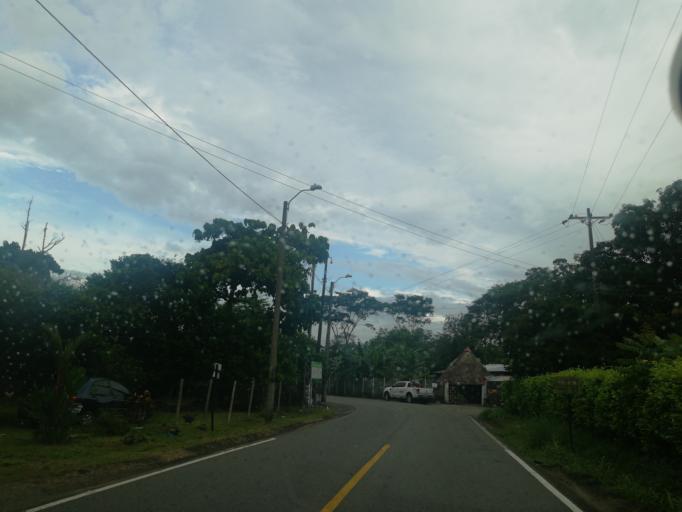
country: CO
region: Meta
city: Acacias
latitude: 3.9879
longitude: -73.7305
